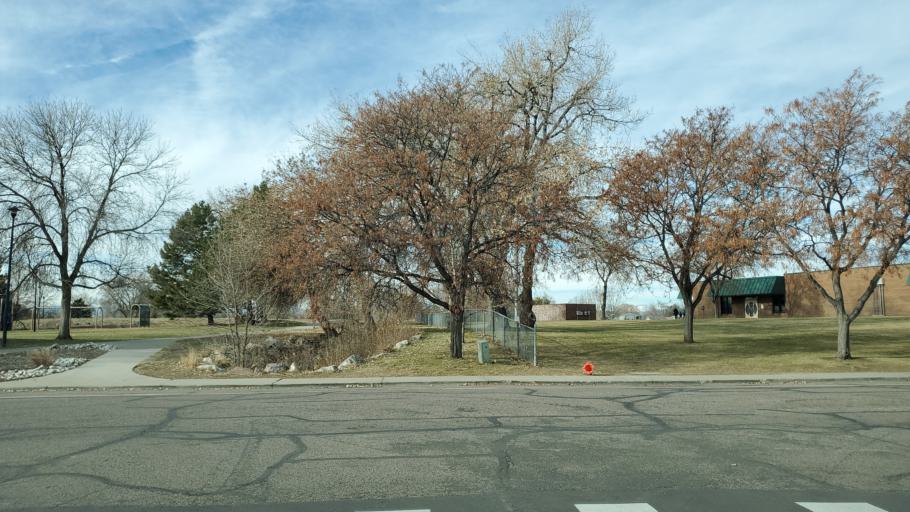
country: US
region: Colorado
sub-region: Adams County
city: Northglenn
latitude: 39.9072
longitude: -104.9454
